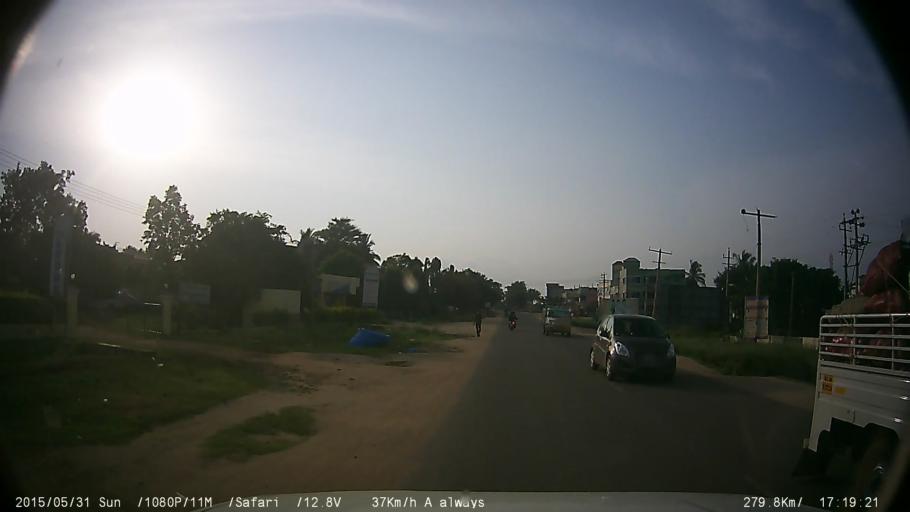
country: IN
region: Karnataka
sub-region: Chamrajnagar
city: Gundlupet
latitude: 11.8153
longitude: 76.6854
